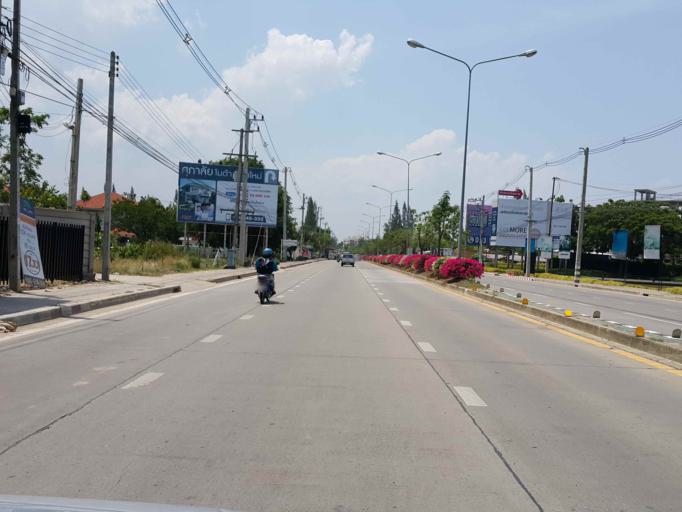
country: TH
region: Chiang Mai
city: San Sai
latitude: 18.8409
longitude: 98.9982
